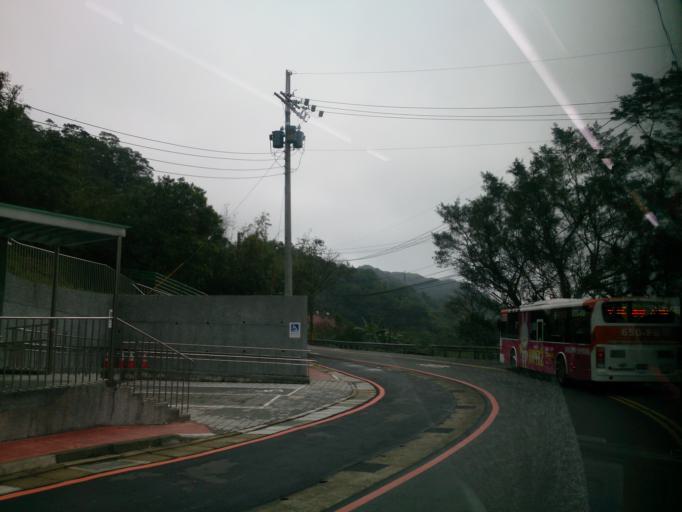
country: TW
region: Taiwan
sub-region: Keelung
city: Keelung
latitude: 25.0208
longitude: 121.7156
